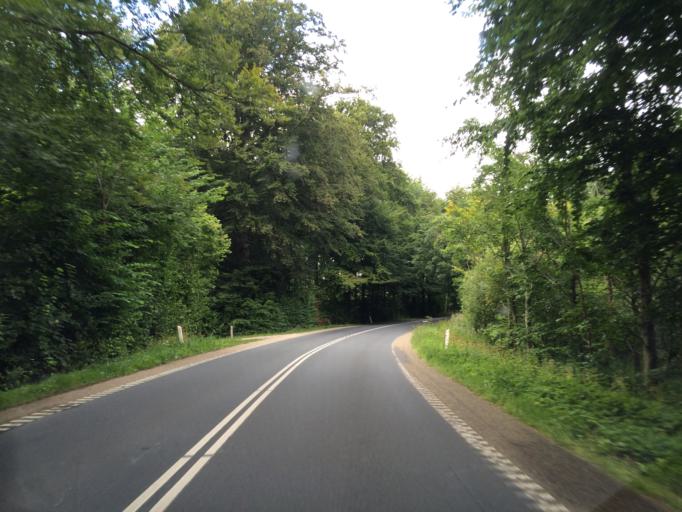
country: DK
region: South Denmark
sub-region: Assens Kommune
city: Harby
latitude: 55.1713
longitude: 10.1454
